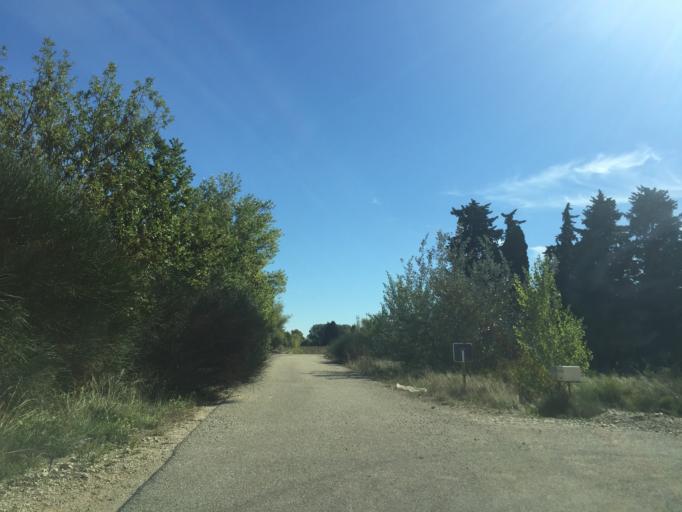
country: FR
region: Provence-Alpes-Cote d'Azur
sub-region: Departement du Vaucluse
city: Piolenc
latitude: 44.1493
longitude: 4.7519
